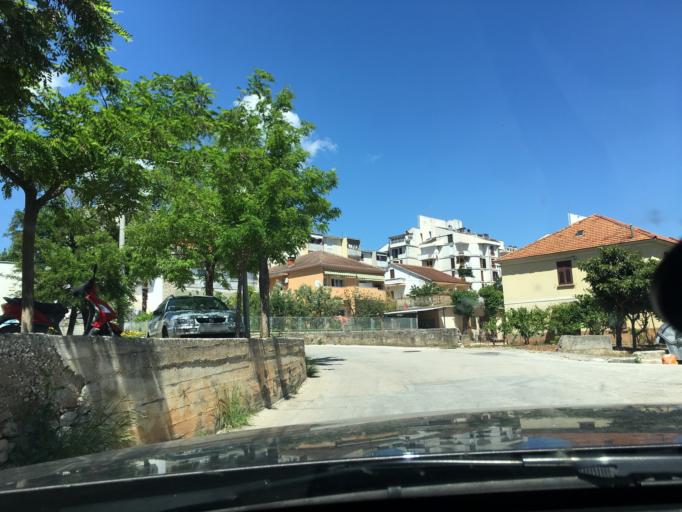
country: HR
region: Splitsko-Dalmatinska
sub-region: Grad Trogir
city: Trogir
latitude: 43.5201
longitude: 16.2543
